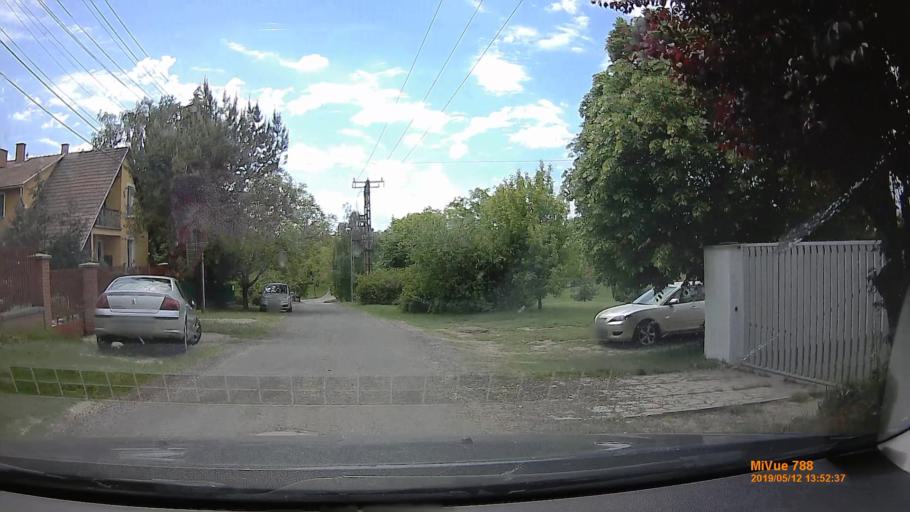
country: HU
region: Pest
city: Pecel
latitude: 47.4883
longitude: 19.3012
